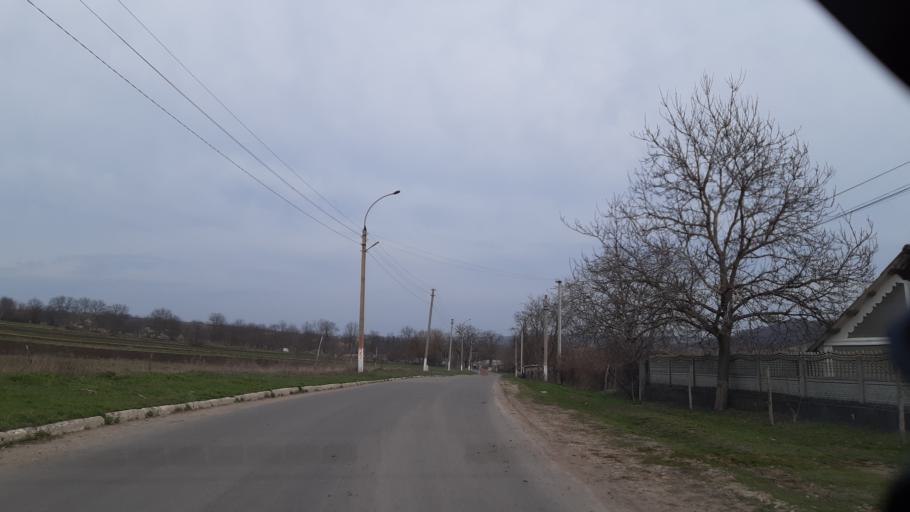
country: MD
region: Soldanesti
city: Soldanesti
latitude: 47.6863
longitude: 28.7493
